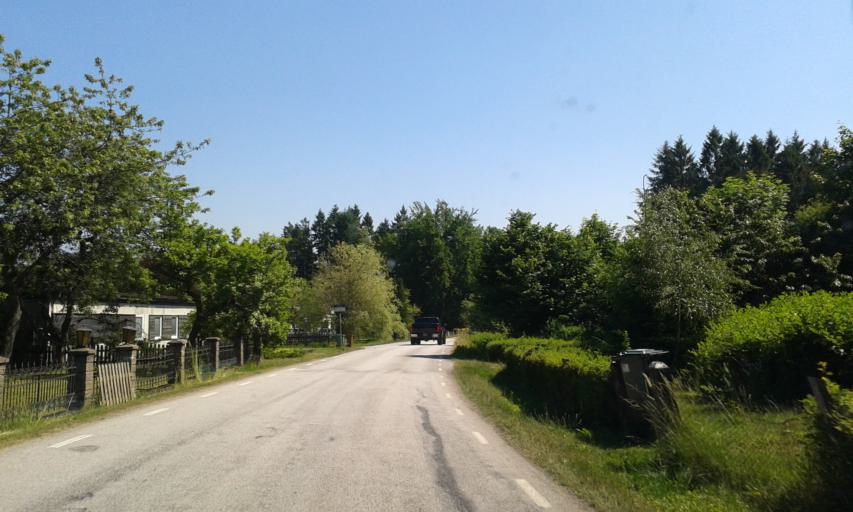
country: SE
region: Blekinge
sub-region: Karlskrona Kommun
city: Rodeby
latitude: 56.2419
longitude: 15.5619
